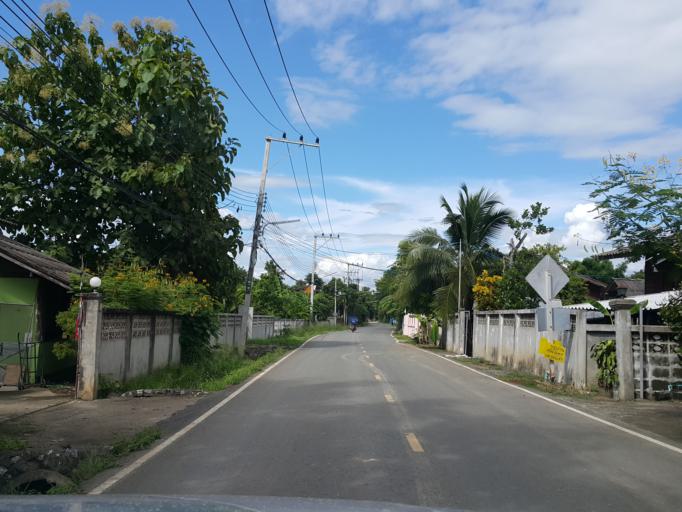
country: TH
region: Chiang Mai
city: San Kamphaeng
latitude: 18.7821
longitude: 99.1300
